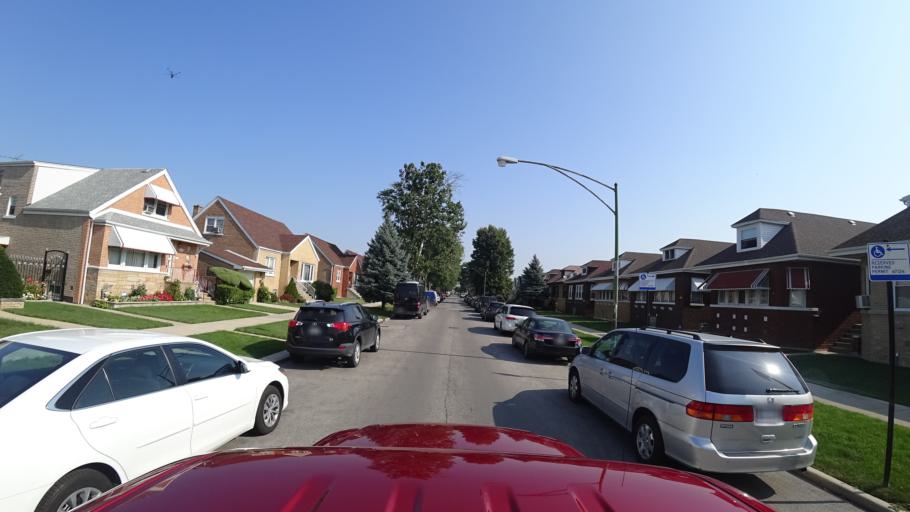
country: US
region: Illinois
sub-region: Cook County
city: Cicero
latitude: 41.8124
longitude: -87.7102
